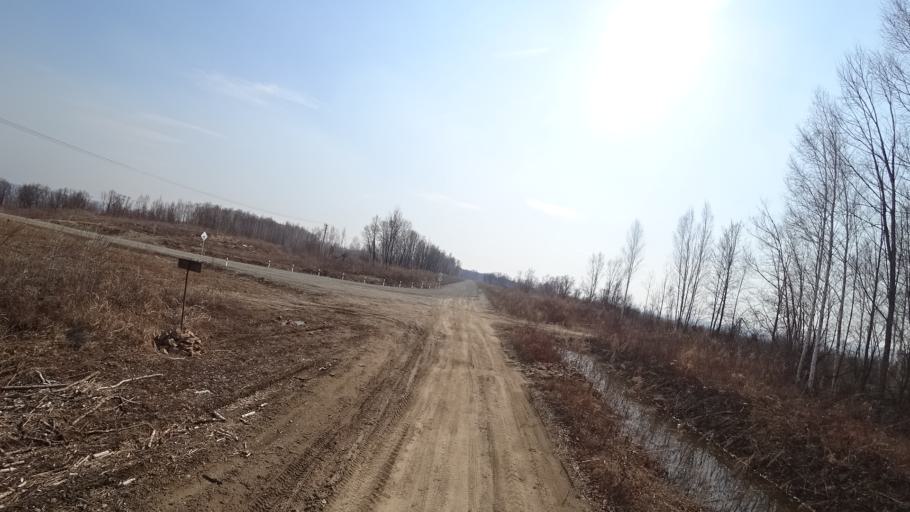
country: RU
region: Amur
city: Novobureyskiy
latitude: 49.8281
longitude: 129.9890
